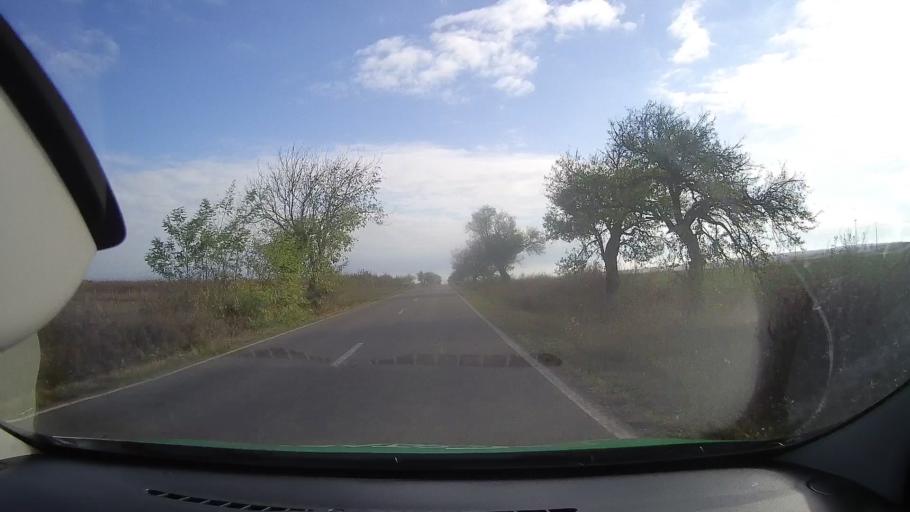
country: RO
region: Tulcea
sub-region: Comuna Mahmudia
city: Mahmudia
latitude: 45.0776
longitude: 29.0642
